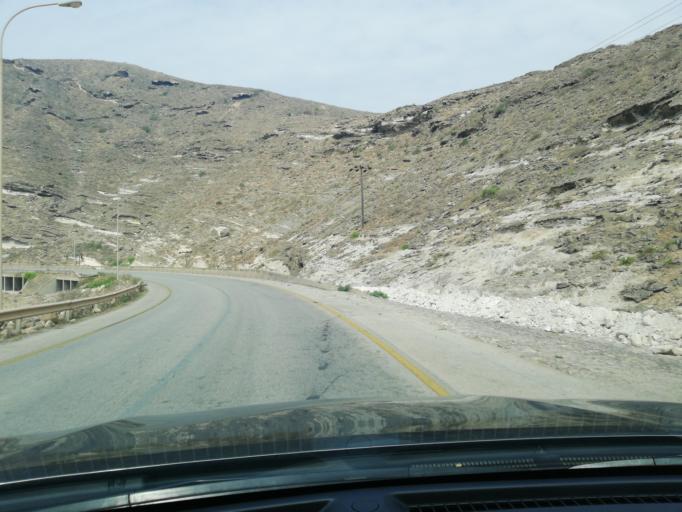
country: OM
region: Zufar
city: Salalah
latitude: 16.8986
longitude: 53.8159
